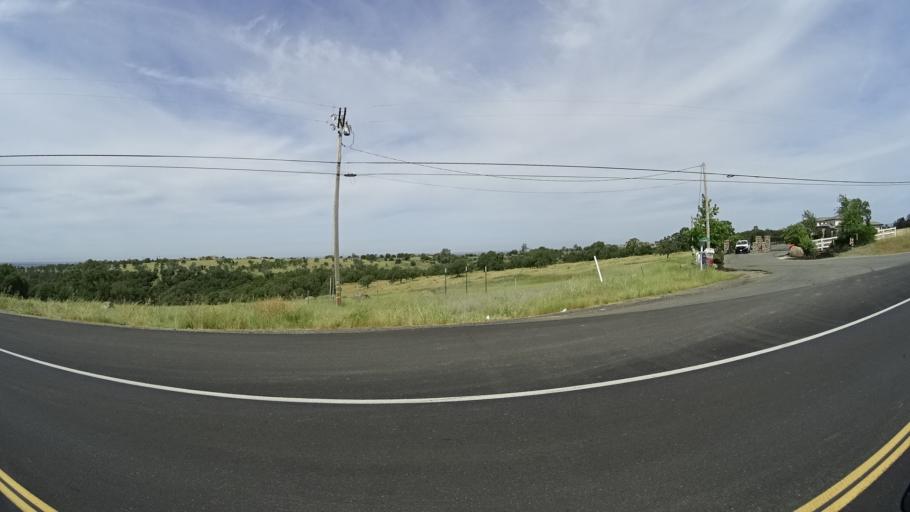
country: US
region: California
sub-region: Placer County
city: Loomis
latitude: 38.8513
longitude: -121.2216
